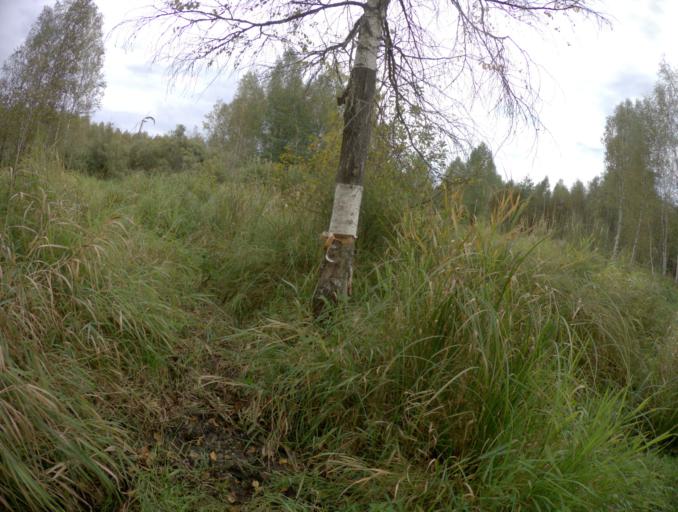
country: RU
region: Vladimir
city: Urshel'skiy
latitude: 55.8211
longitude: 40.2744
